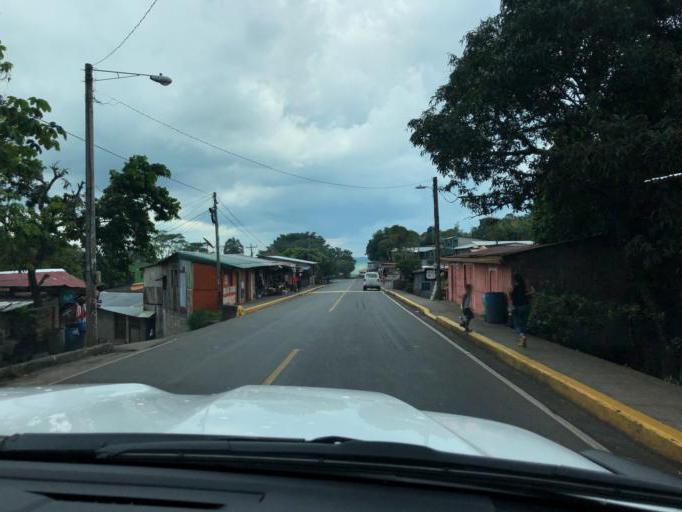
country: NI
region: Chontales
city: Villa Sandino
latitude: 11.9986
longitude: -84.7797
